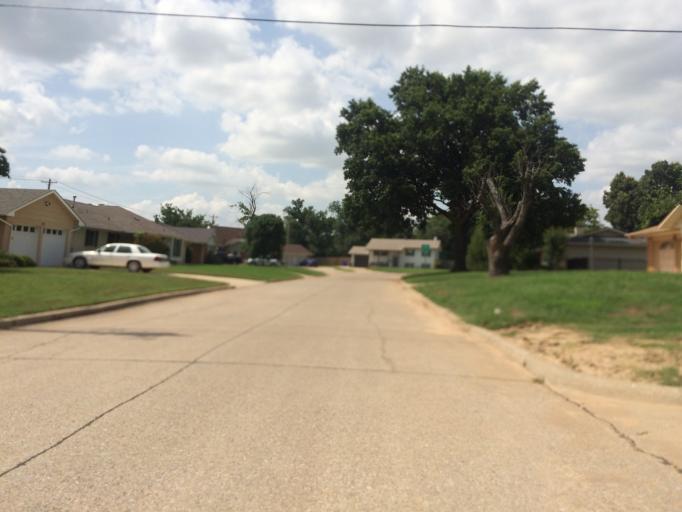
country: US
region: Oklahoma
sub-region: Cleveland County
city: Norman
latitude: 35.2136
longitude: -97.4835
